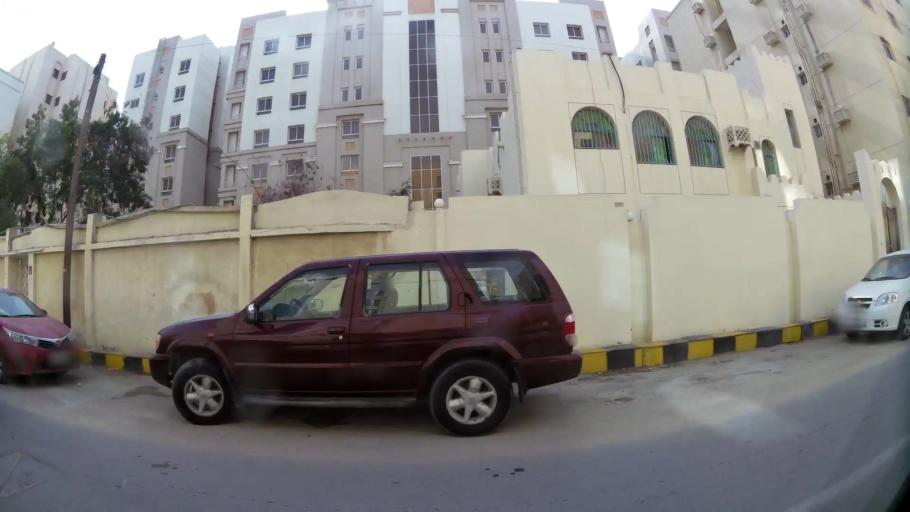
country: QA
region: Baladiyat ad Dawhah
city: Doha
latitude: 25.2777
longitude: 51.5096
